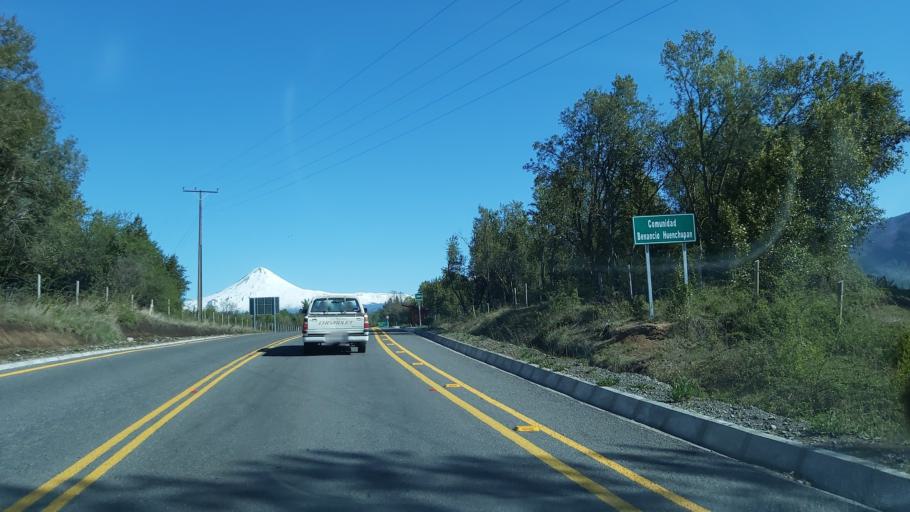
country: CL
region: Araucania
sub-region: Provincia de Cautin
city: Vilcun
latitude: -38.4903
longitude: -71.8254
